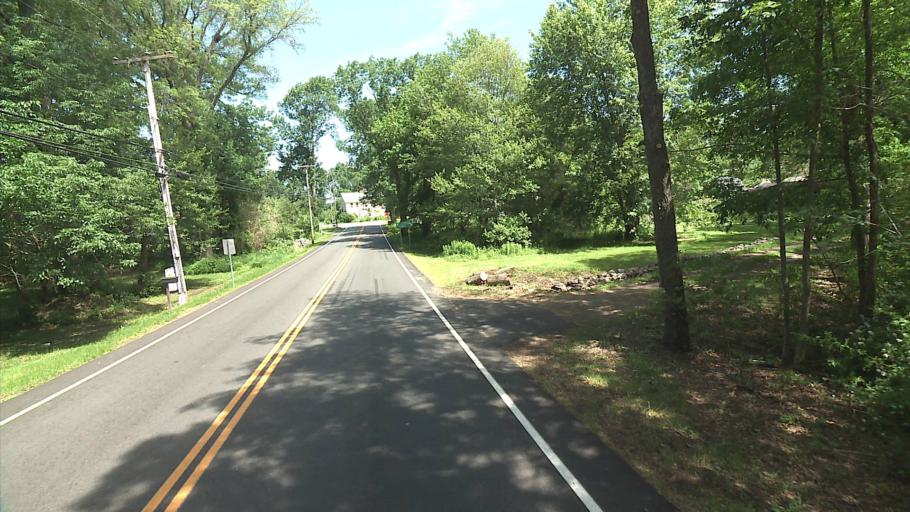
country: US
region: Connecticut
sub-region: Windham County
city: Moosup
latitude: 41.6878
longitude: -71.8498
